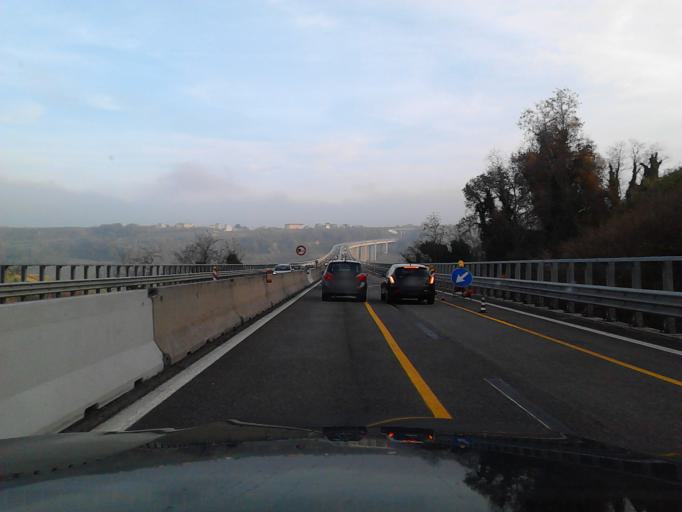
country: IT
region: Abruzzo
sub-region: Provincia di Chieti
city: Ortona
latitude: 42.3144
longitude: 14.4082
